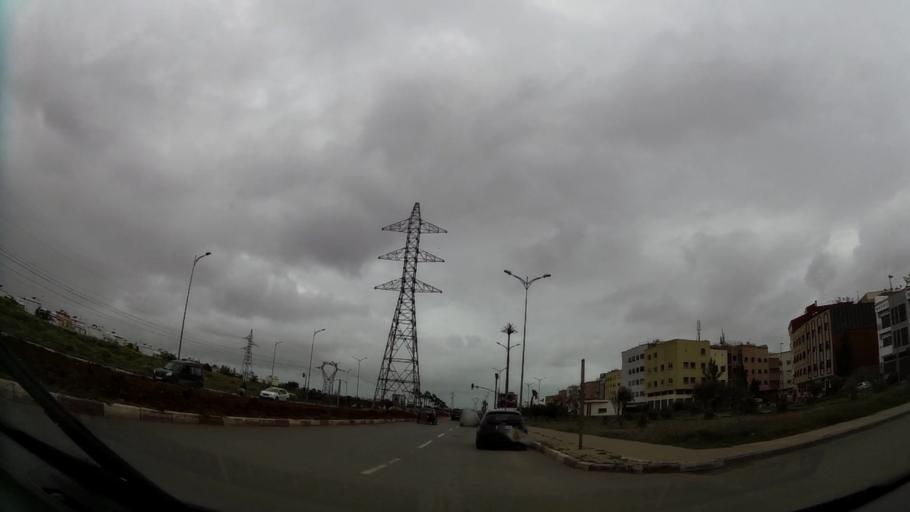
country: MA
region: Grand Casablanca
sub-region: Casablanca
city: Casablanca
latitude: 33.5308
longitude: -7.6171
